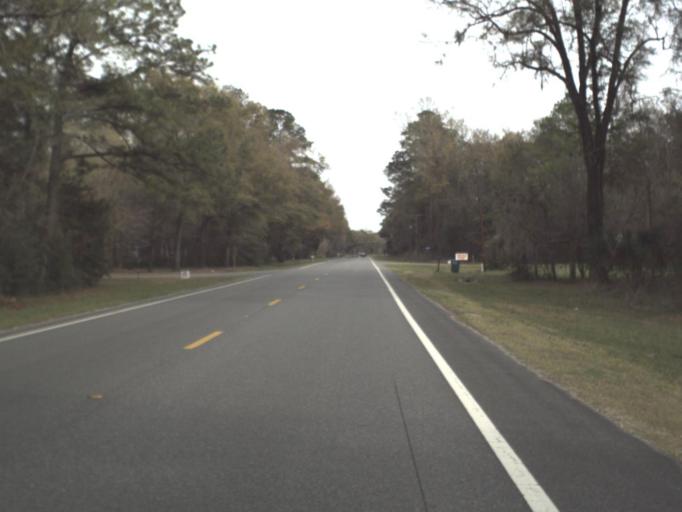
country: US
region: Florida
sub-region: Leon County
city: Woodville
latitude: 30.2378
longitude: -84.2588
